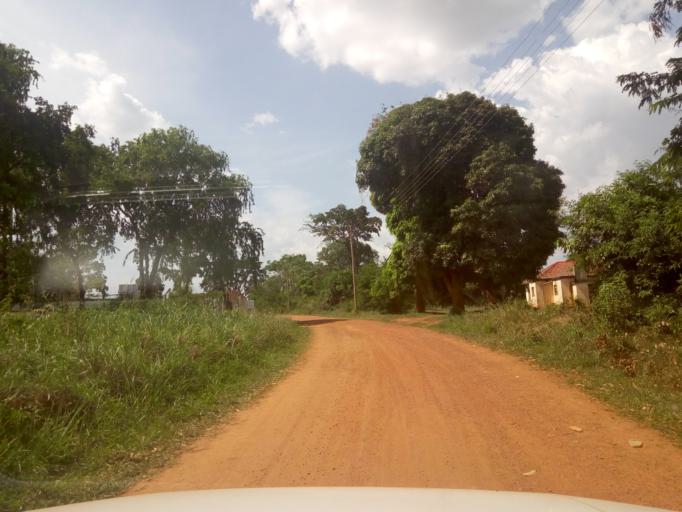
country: UG
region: Western Region
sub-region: Masindi District
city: Masindi
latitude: 1.6913
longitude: 31.7243
